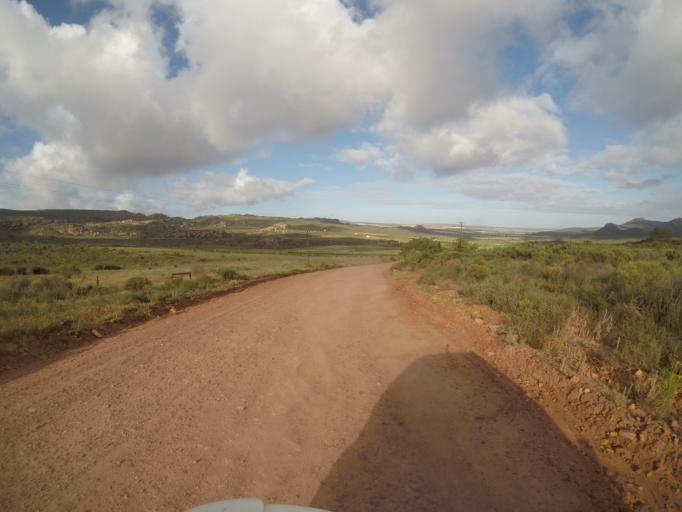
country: ZA
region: Western Cape
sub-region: West Coast District Municipality
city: Clanwilliam
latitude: -32.3438
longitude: 18.7566
